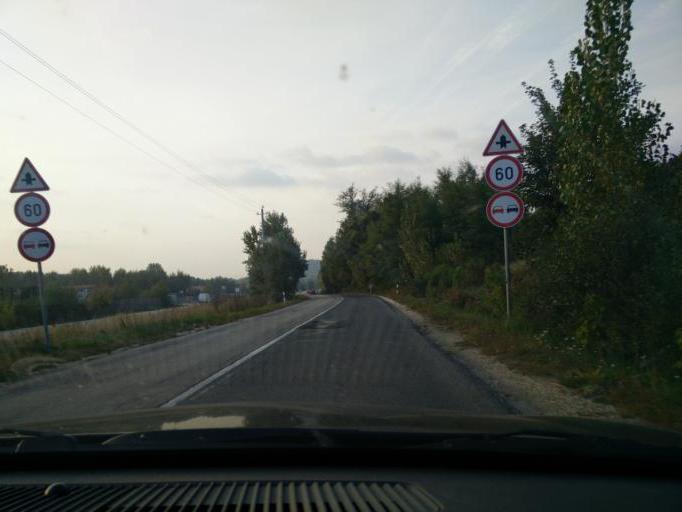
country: HU
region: Pest
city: Piliscsaba
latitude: 47.6431
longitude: 18.8096
